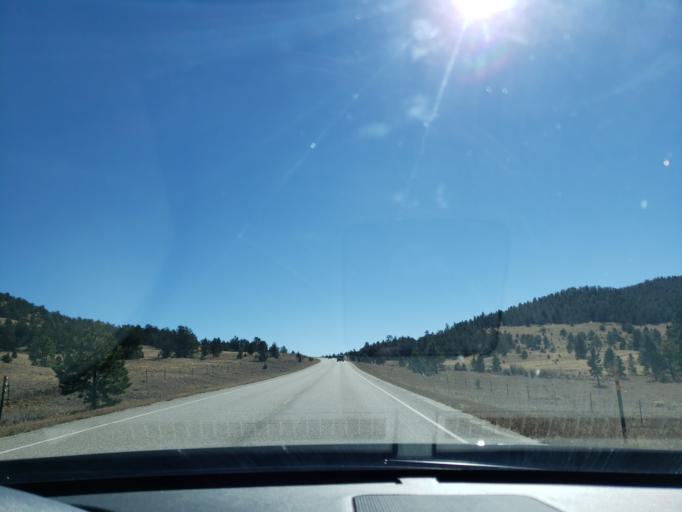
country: US
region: Colorado
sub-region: Chaffee County
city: Salida
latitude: 38.8428
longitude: -105.6411
